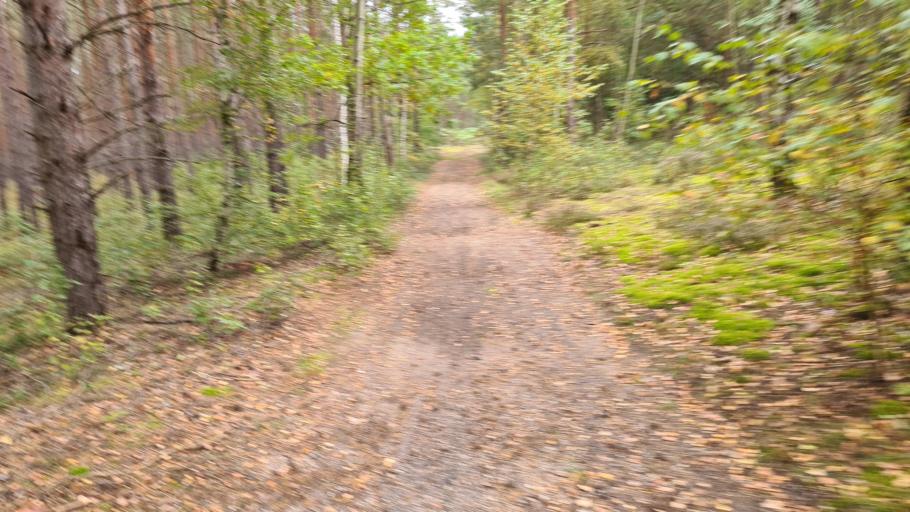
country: DE
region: Brandenburg
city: Doberlug-Kirchhain
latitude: 51.6295
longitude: 13.6105
